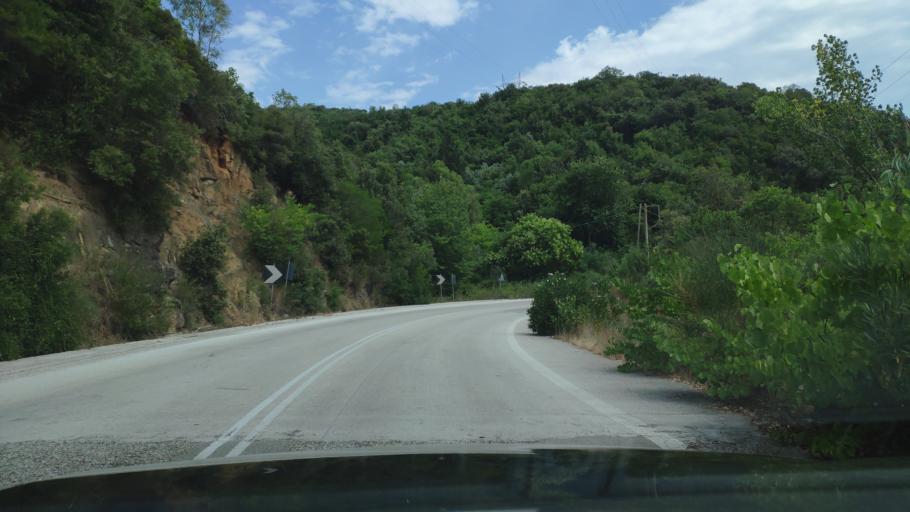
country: GR
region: West Greece
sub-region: Nomos Aitolias kai Akarnanias
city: Menidi
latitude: 39.0263
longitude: 21.1324
